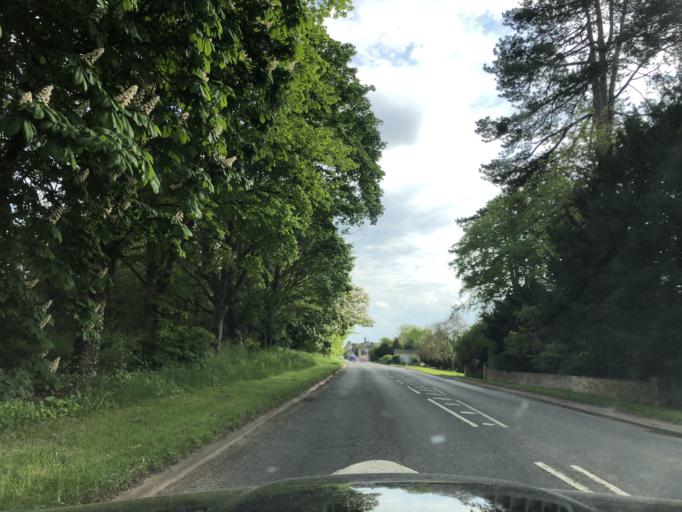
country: GB
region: England
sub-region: Warwickshire
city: Shipston on Stour
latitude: 52.1099
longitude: -1.6197
